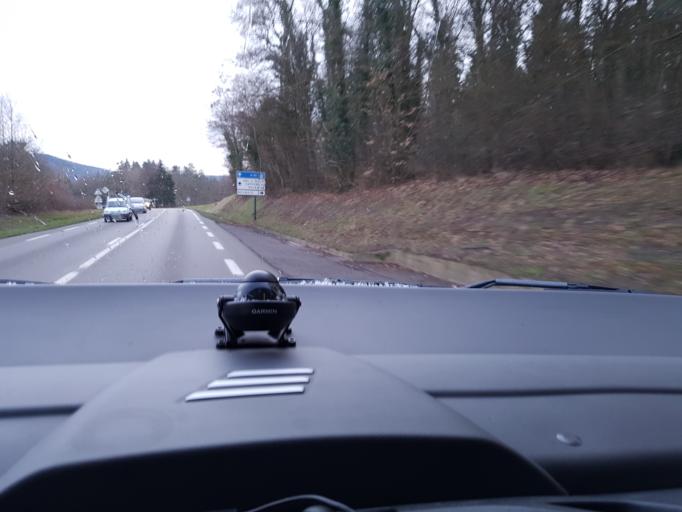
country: FR
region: Alsace
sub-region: Departement du Bas-Rhin
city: Chatenois
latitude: 48.3017
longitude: 7.3549
